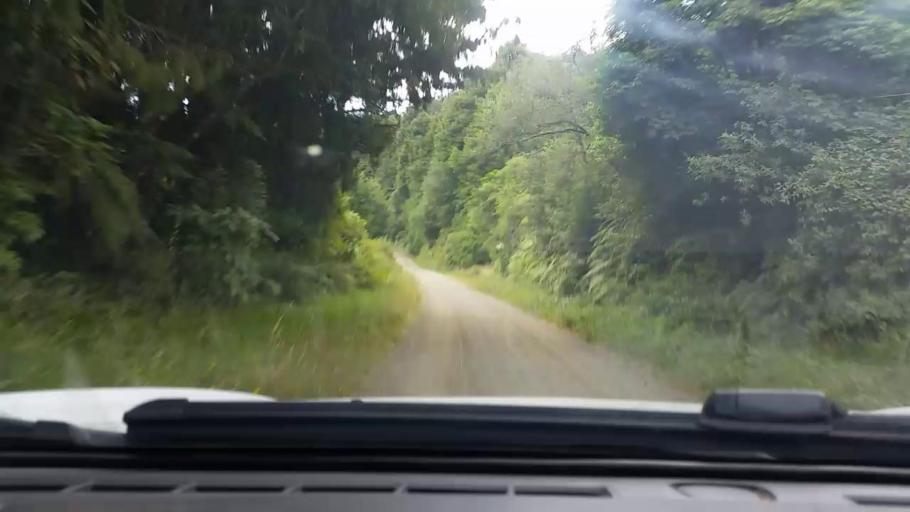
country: NZ
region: Bay of Plenty
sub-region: Kawerau District
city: Kawerau
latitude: -38.0080
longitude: 176.5986
